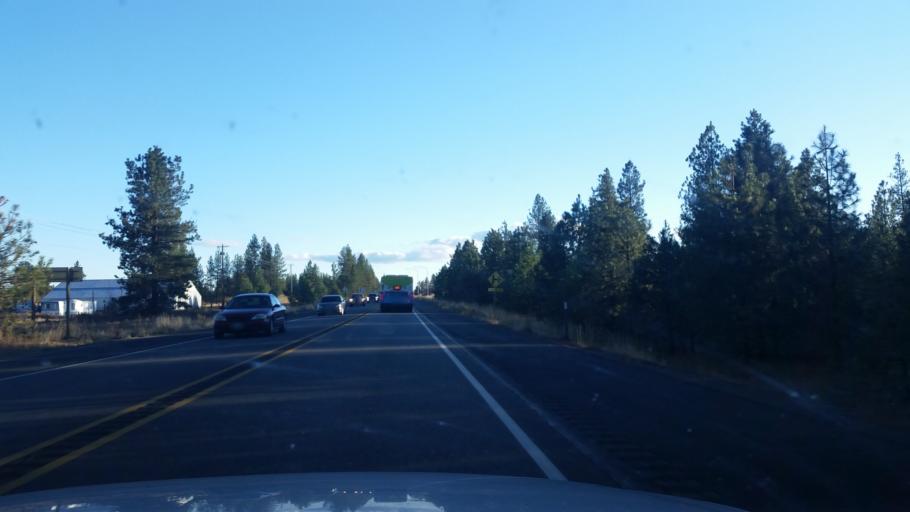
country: US
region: Washington
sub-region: Spokane County
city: Cheney
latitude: 47.5167
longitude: -117.5646
